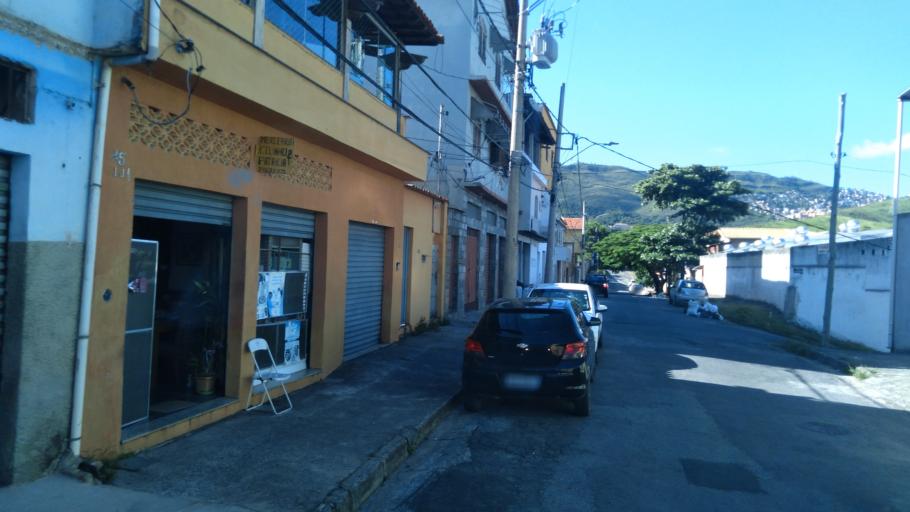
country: BR
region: Minas Gerais
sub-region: Belo Horizonte
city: Belo Horizonte
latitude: -19.9200
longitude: -43.8968
